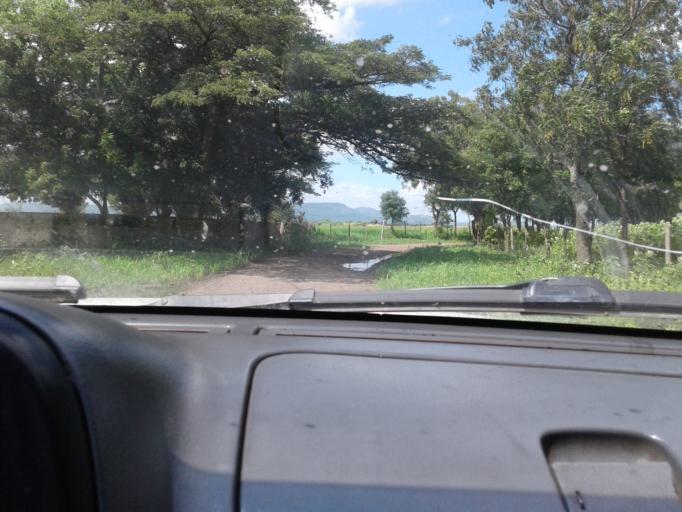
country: NI
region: Matagalpa
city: Ciudad Dario
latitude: 12.8433
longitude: -86.1437
